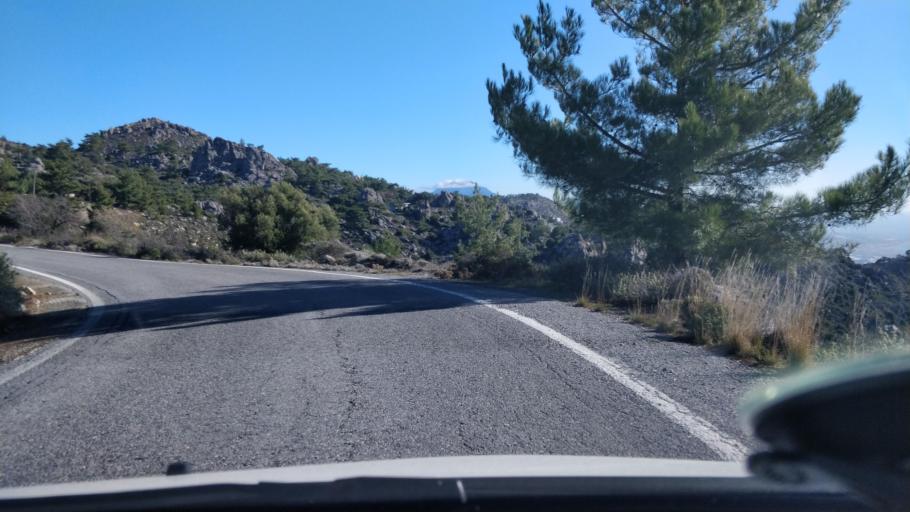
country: GR
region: Crete
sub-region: Nomos Lasithiou
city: Gra Liyia
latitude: 35.0439
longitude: 25.6344
